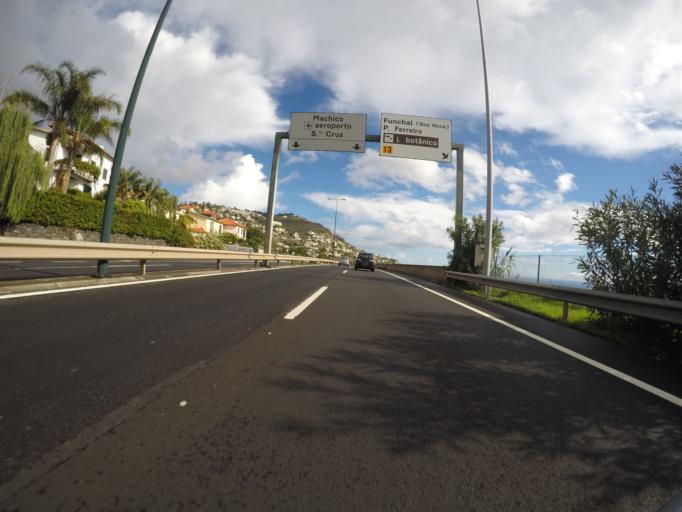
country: PT
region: Madeira
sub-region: Funchal
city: Nossa Senhora do Monte
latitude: 32.6579
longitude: -16.8873
